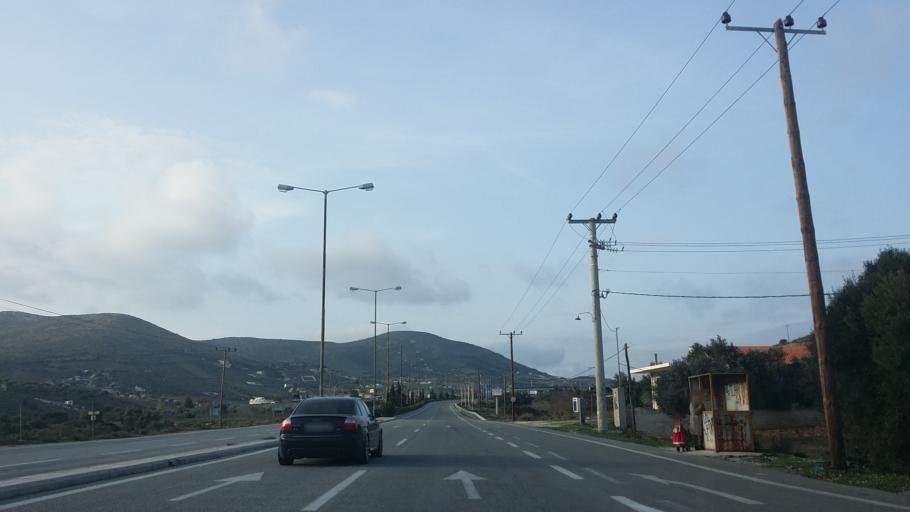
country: GR
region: Attica
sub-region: Nomarchia Anatolikis Attikis
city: Lavrio
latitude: 37.7681
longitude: 24.0557
